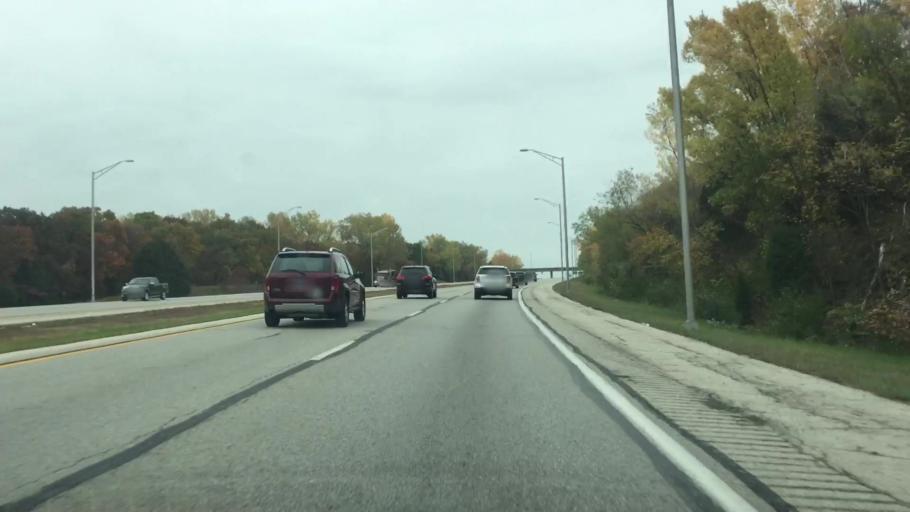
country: US
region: Kansas
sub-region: Wyandotte County
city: Edwardsville
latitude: 39.0103
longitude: -94.7999
